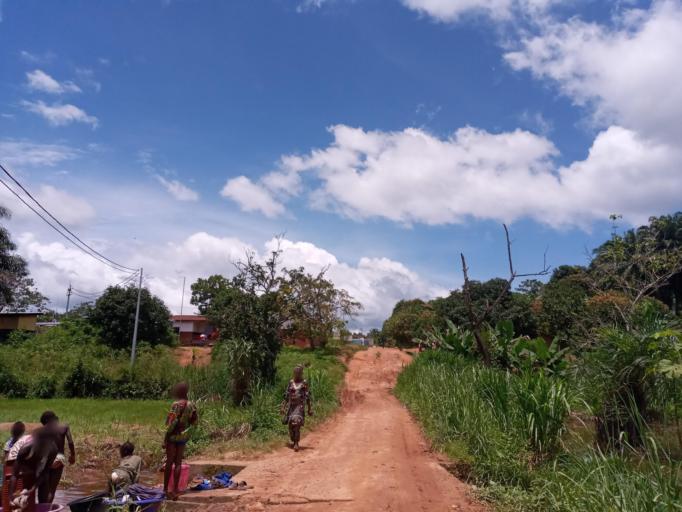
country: SL
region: Eastern Province
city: Tombu
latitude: 8.6270
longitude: -10.8234
